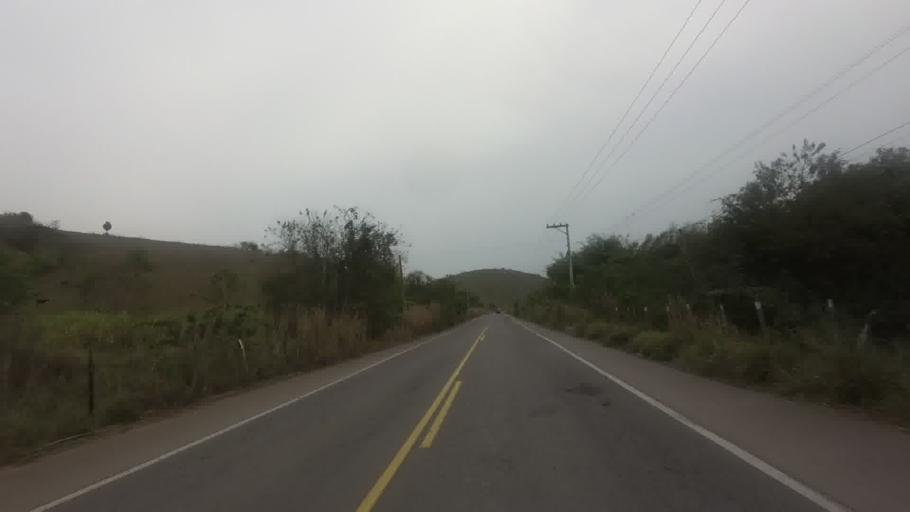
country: BR
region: Rio de Janeiro
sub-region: Santo Antonio De Padua
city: Santo Antonio de Padua
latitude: -21.6016
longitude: -42.2371
